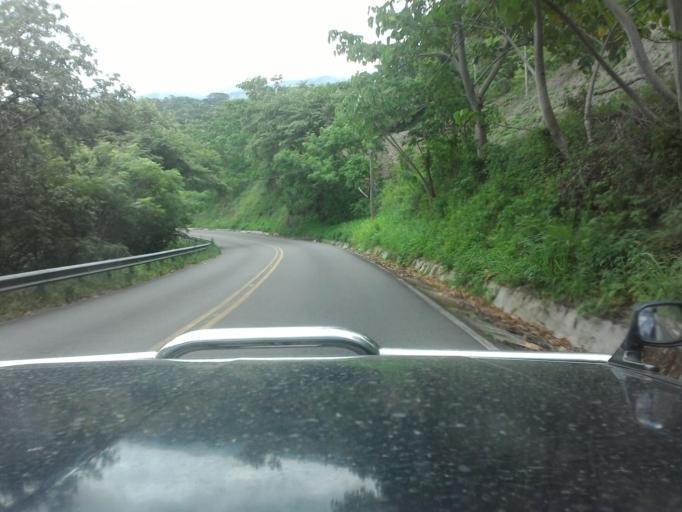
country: CR
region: Puntarenas
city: Miramar
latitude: 10.1842
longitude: -84.8358
